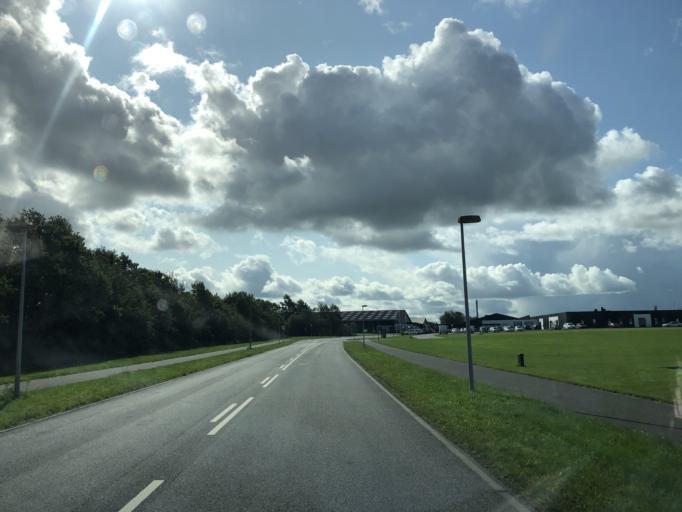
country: DK
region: Central Jutland
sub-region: Herning Kommune
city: Lind
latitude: 56.1125
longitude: 8.9792
